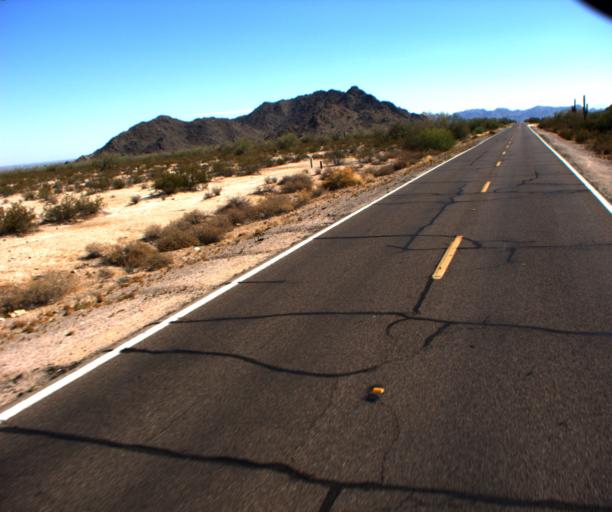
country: US
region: Arizona
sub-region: Pinal County
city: Sacaton
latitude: 33.0266
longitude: -111.7378
